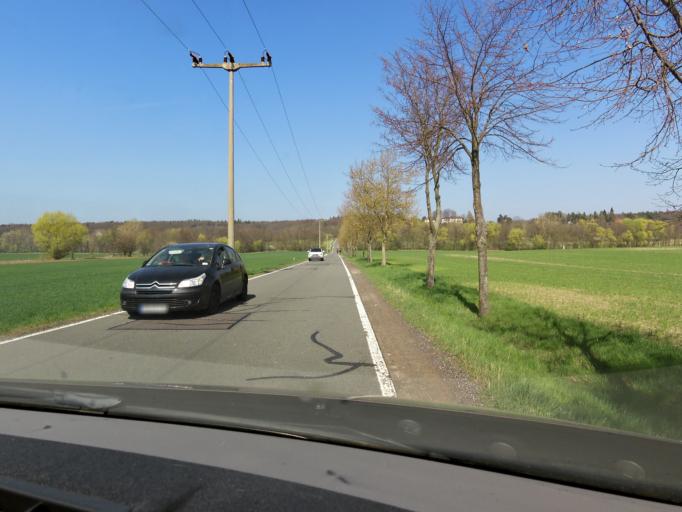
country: DE
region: Thuringia
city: Ernstroda
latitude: 50.8932
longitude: 10.6518
